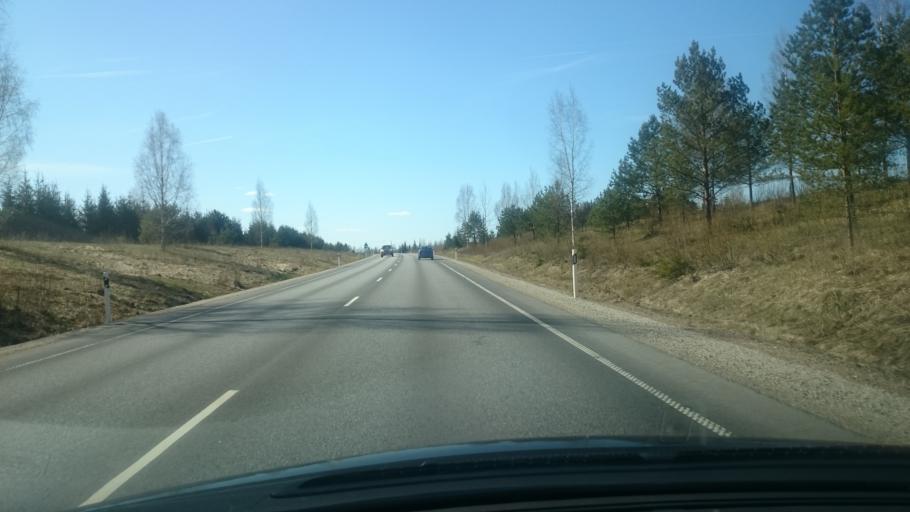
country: EE
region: Tartu
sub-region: UElenurme vald
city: Ulenurme
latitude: 58.3481
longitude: 26.9369
